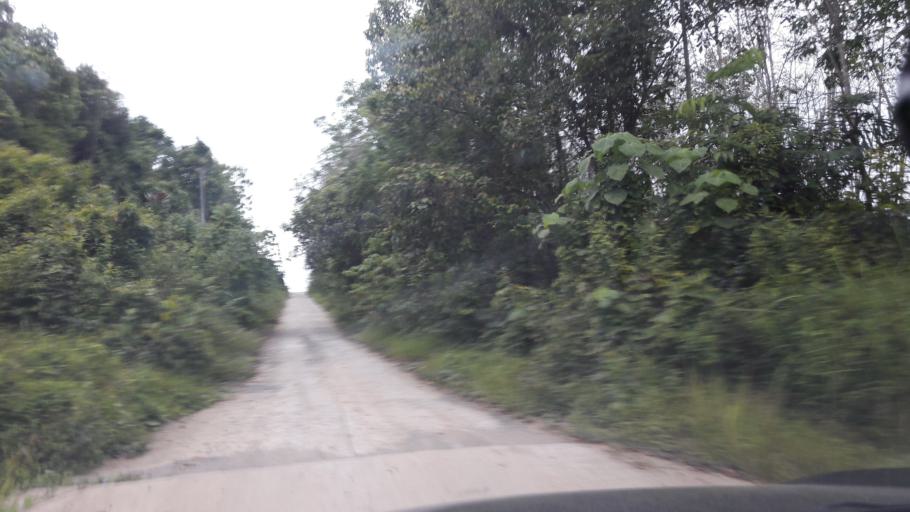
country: ID
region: South Sumatra
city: Gunungmenang
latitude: -3.1965
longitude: 103.8081
